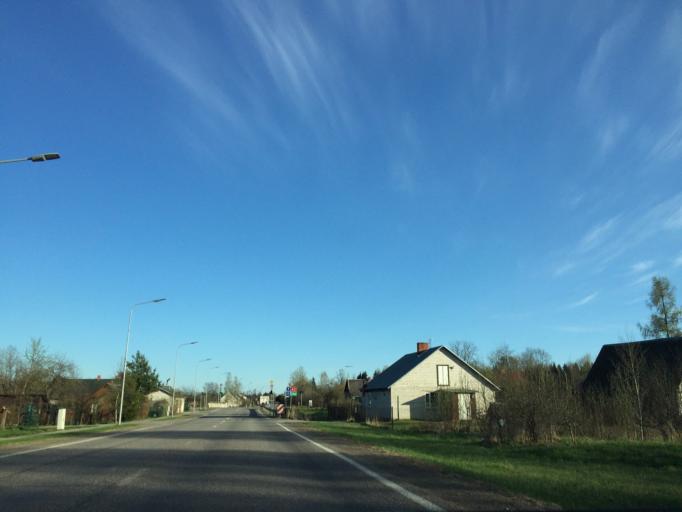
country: LV
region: Valkas Rajons
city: Valka
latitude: 57.7714
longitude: 25.9985
